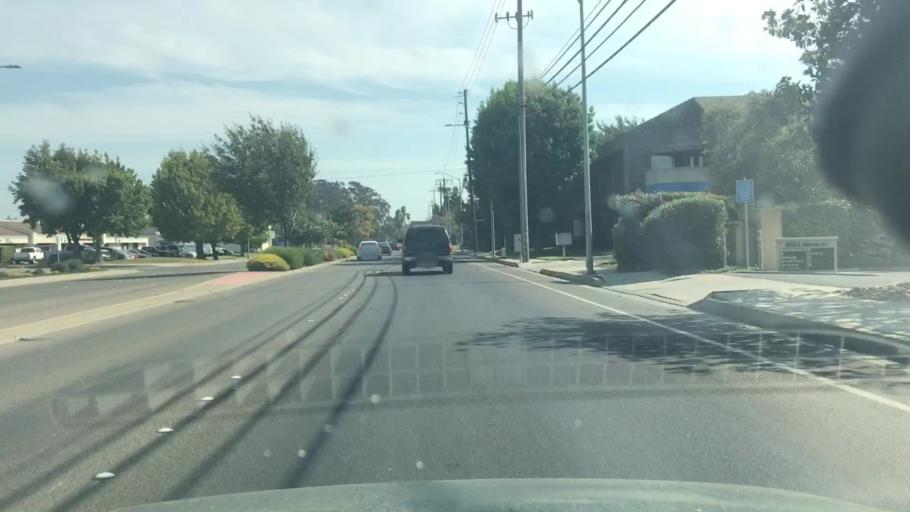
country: US
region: California
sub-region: Santa Barbara County
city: Santa Maria
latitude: 34.9193
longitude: -120.4542
